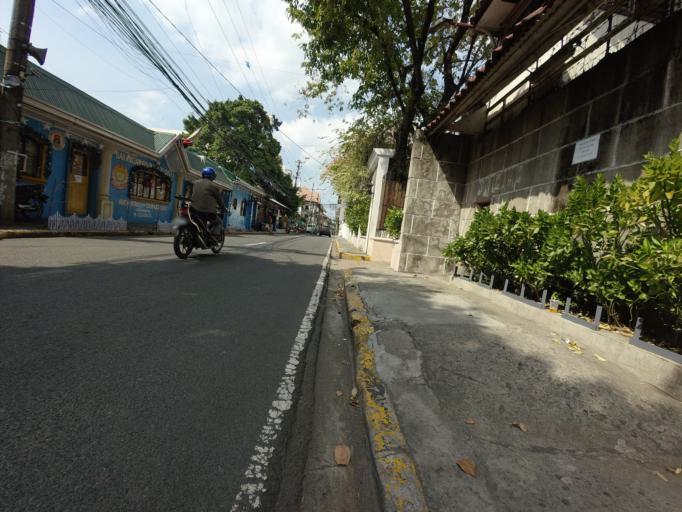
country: PH
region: Metro Manila
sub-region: City of Manila
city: Port Area
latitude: 14.5887
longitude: 120.9769
